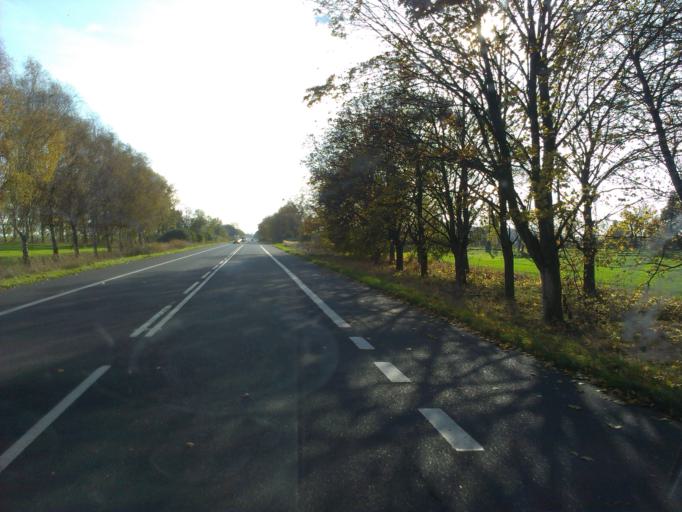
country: PL
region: West Pomeranian Voivodeship
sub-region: Powiat pyrzycki
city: Pyrzyce
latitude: 53.1978
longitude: 14.8247
